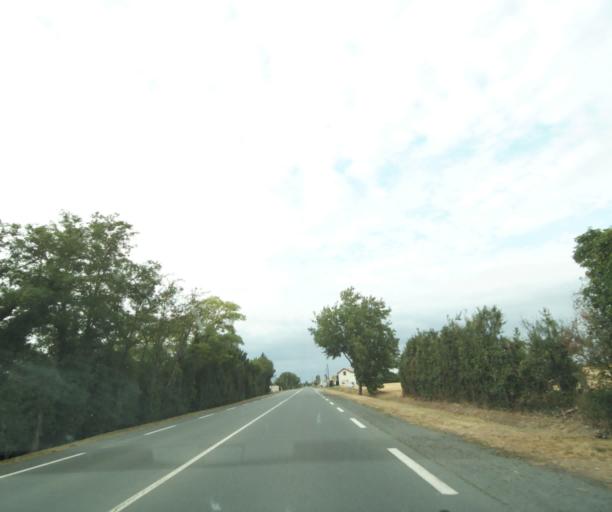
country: FR
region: Poitou-Charentes
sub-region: Departement de la Charente-Maritime
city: Marans
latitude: 46.2977
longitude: -0.9909
